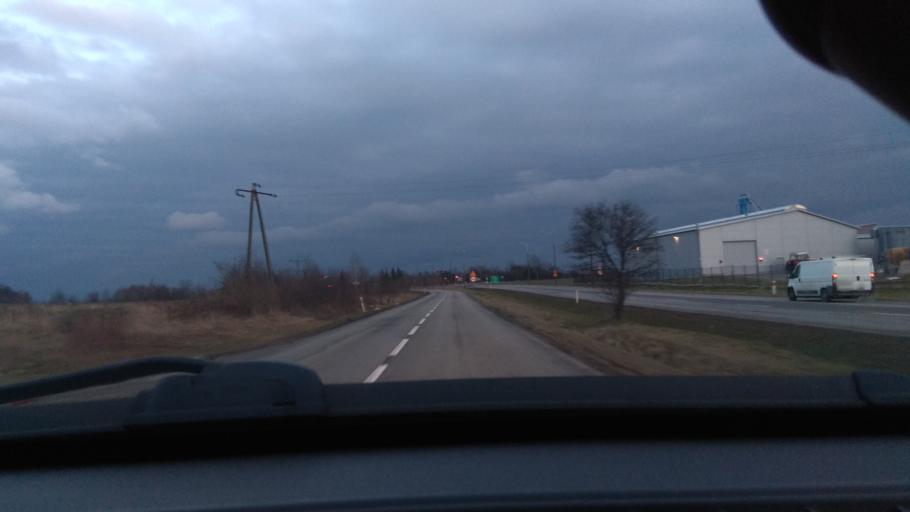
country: PL
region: Greater Poland Voivodeship
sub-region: Powiat kepinski
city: Kepno
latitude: 51.2882
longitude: 18.0101
